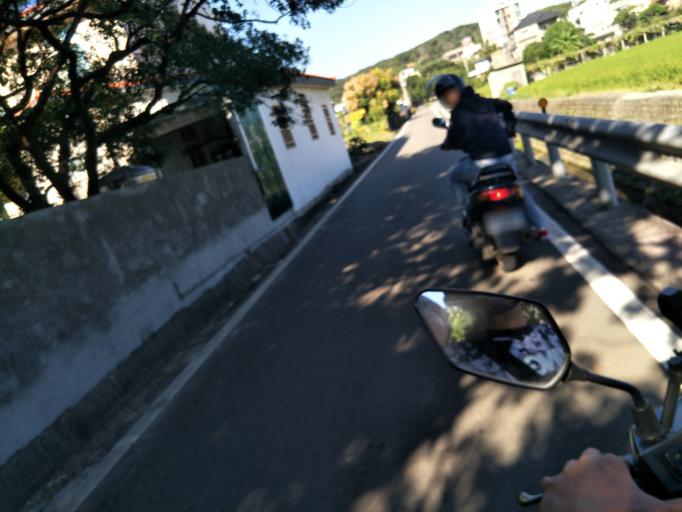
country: TW
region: Taiwan
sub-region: Hsinchu
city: Zhubei
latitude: 24.8410
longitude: 121.0367
